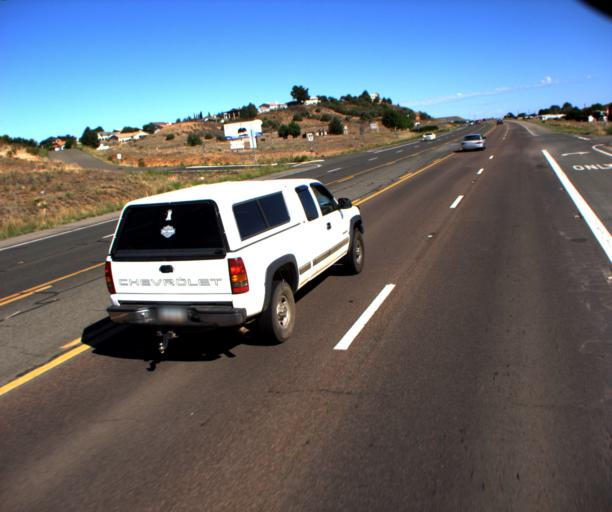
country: US
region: Arizona
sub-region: Yavapai County
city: Dewey-Humboldt
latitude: 34.5528
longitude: -112.2526
